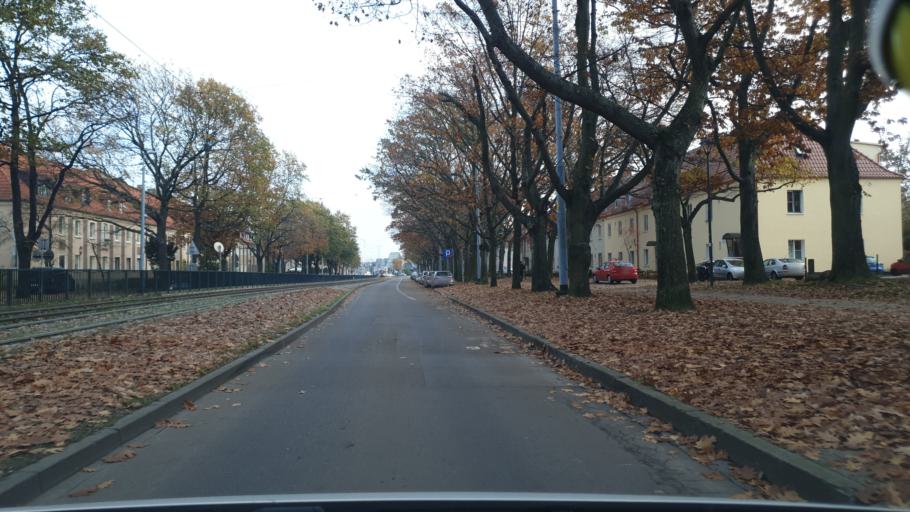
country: PL
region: Pomeranian Voivodeship
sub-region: Sopot
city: Sopot
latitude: 54.3868
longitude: 18.5856
